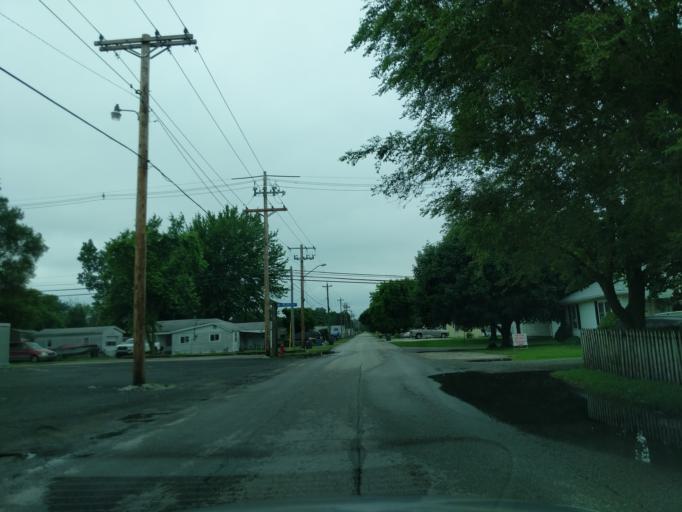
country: US
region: Indiana
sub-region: Tipton County
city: Tipton
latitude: 40.2829
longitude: -86.0498
